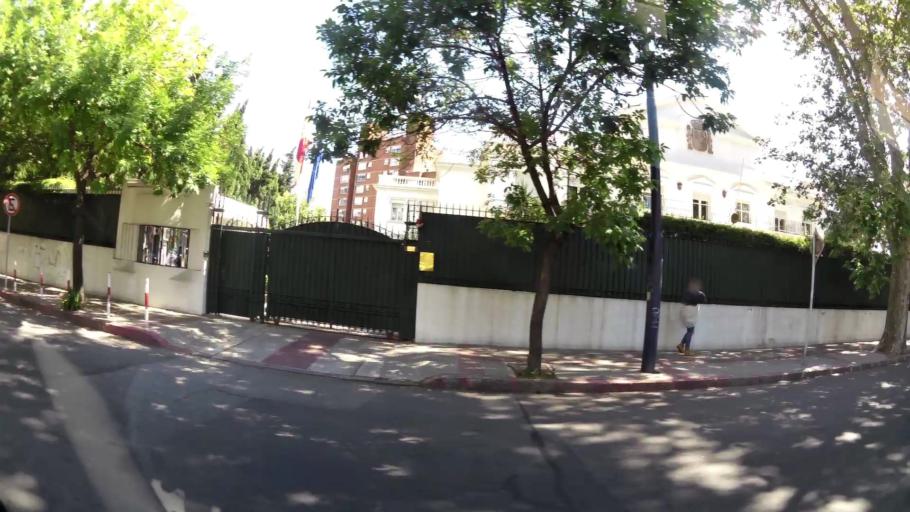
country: UY
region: Montevideo
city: Montevideo
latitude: -34.9091
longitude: -56.1538
